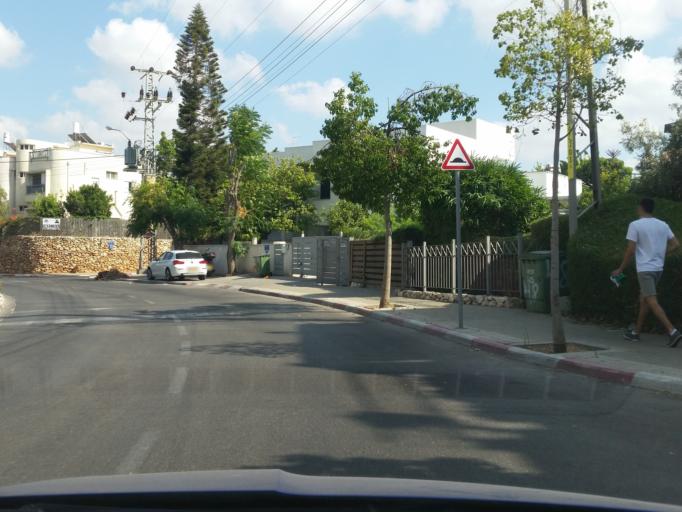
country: IL
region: Tel Aviv
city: Ramat HaSharon
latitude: 32.1155
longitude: 34.8317
